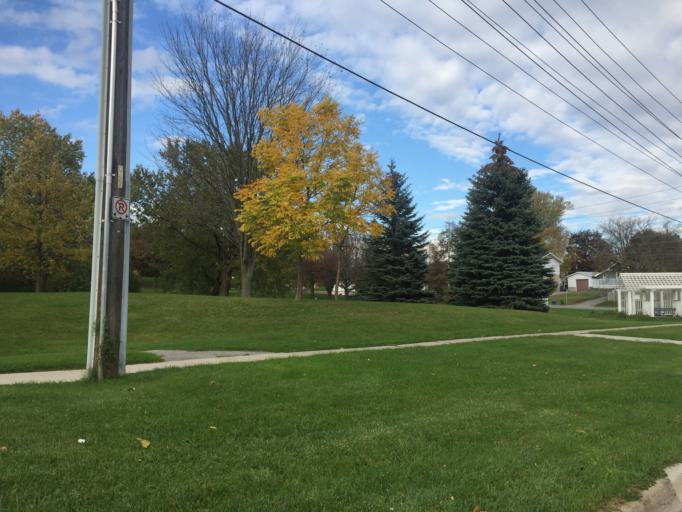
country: CA
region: Ontario
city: Oshawa
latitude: 43.9128
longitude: -78.8605
